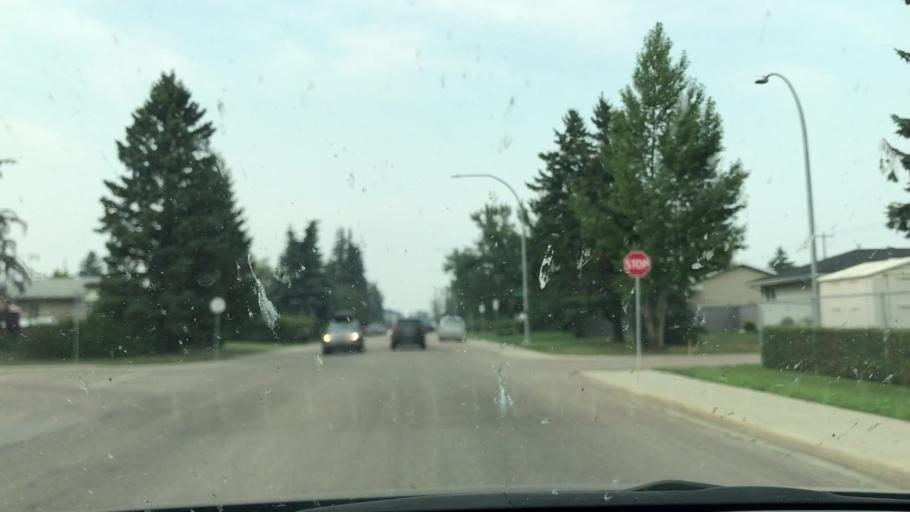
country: CA
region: Alberta
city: St. Albert
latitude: 53.5960
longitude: -113.5534
